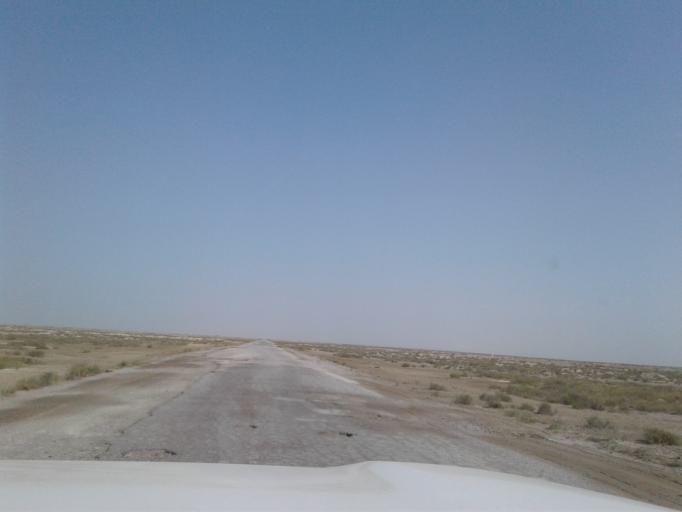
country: IR
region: Golestan
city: Gomishan
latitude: 37.9289
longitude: 53.8457
